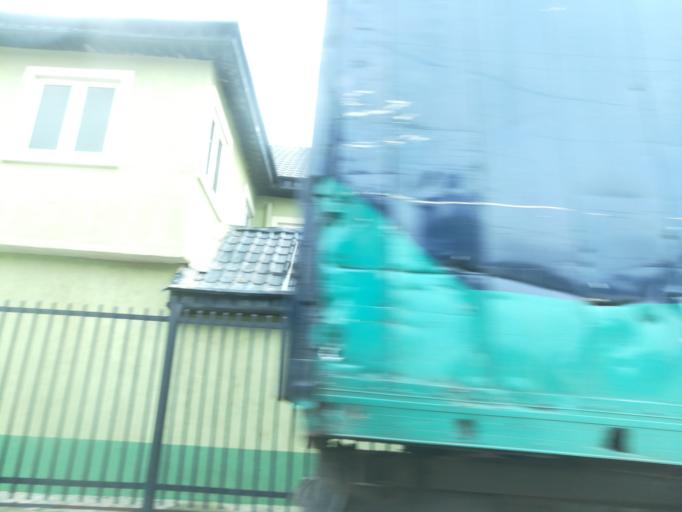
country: NG
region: Lagos
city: Agege
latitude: 6.6065
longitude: 3.3166
